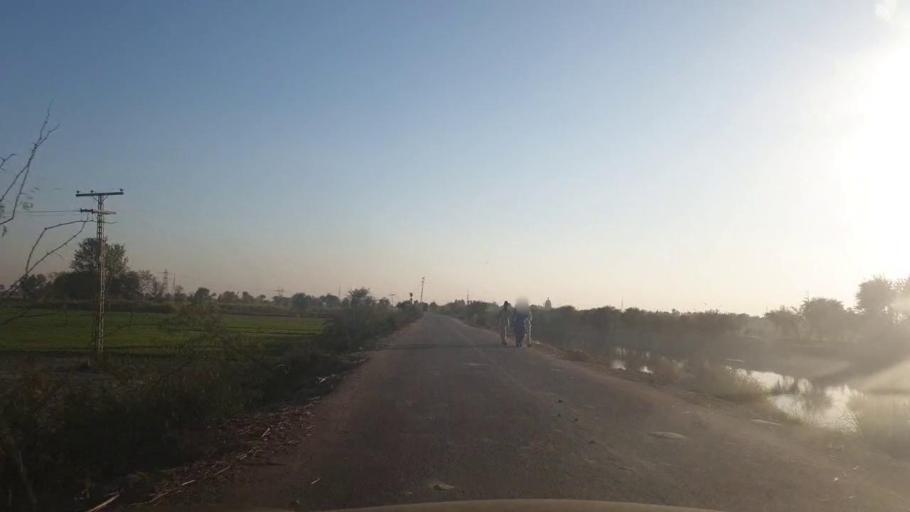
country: PK
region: Sindh
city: Mirpur Mathelo
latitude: 28.0006
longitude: 69.4682
